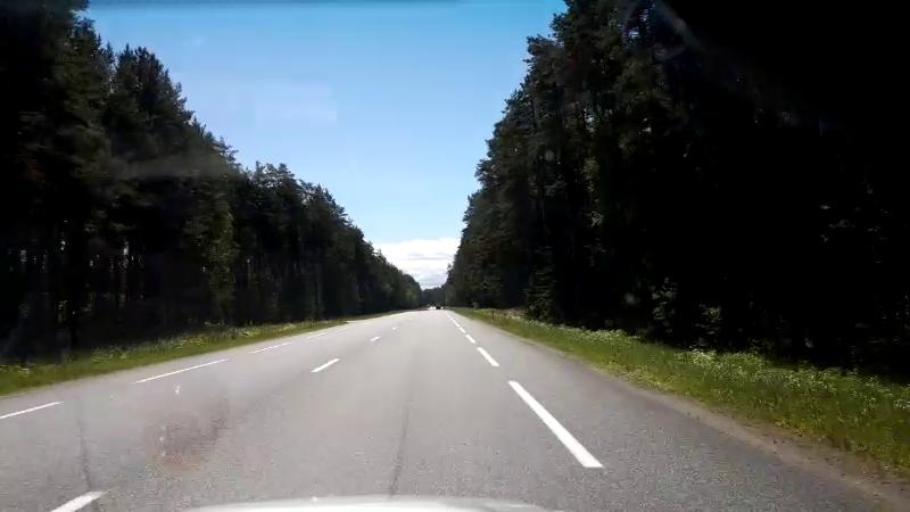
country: LV
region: Saulkrastu
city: Saulkrasti
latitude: 57.3563
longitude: 24.4380
